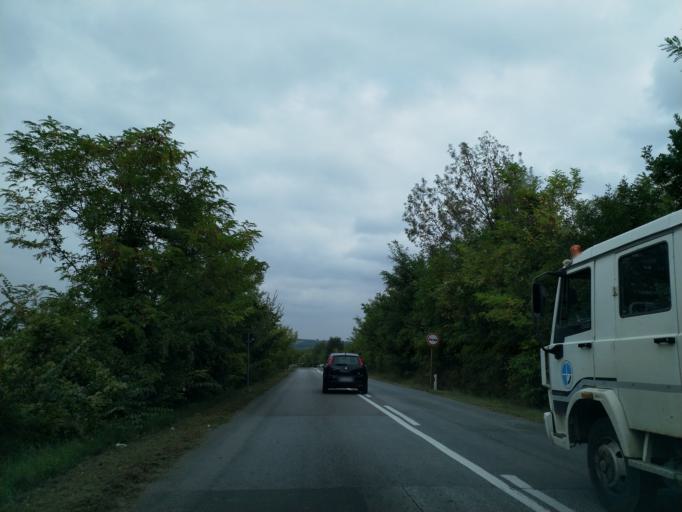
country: RS
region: Central Serbia
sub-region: Sumadijski Okrug
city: Topola
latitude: 44.2046
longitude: 20.7232
